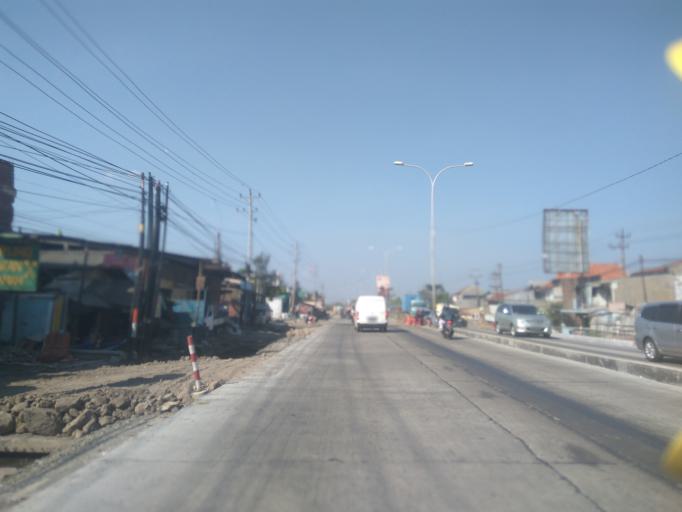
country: ID
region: Central Java
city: Semarang
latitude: -6.9552
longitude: 110.4701
